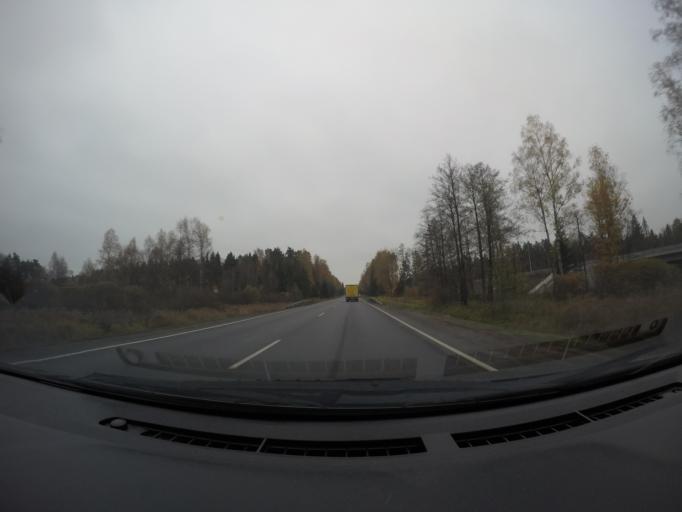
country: RU
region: Moskovskaya
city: Gzhel'
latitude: 55.5598
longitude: 38.3968
